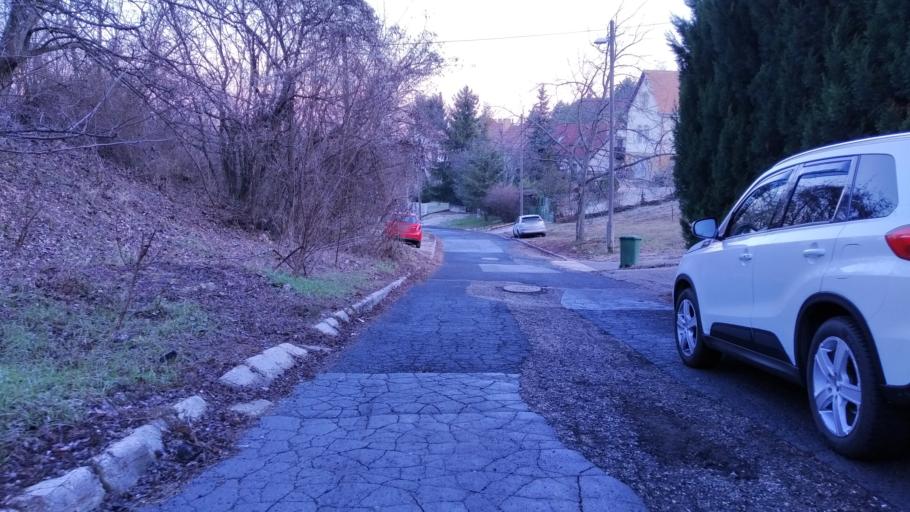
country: HU
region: Budapest
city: Budapest III. keruelet
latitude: 47.5590
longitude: 19.0164
